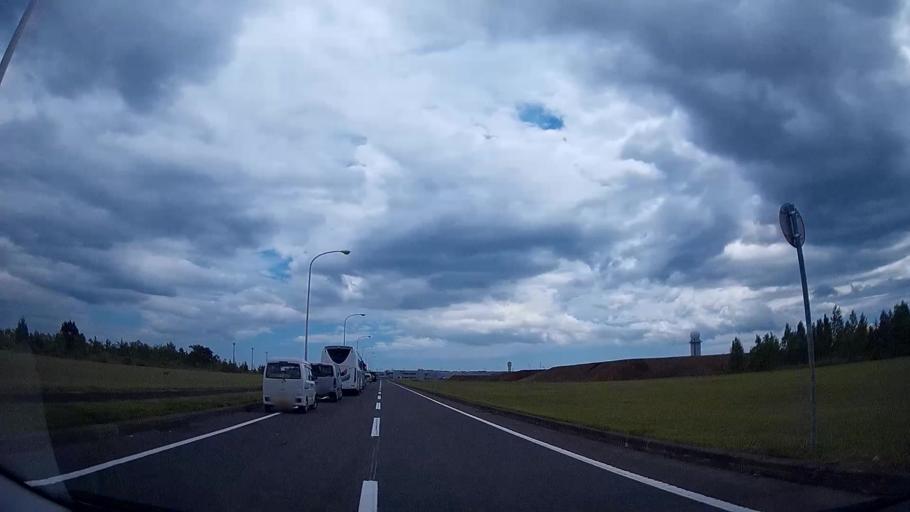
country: JP
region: Hokkaido
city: Chitose
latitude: 42.8006
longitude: 141.6797
